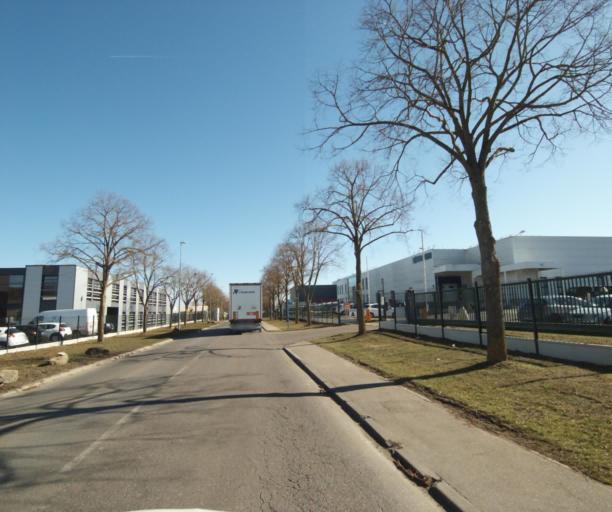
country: FR
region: Lorraine
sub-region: Departement de Meurthe-et-Moselle
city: Fleville-devant-Nancy
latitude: 48.6153
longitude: 6.1870
